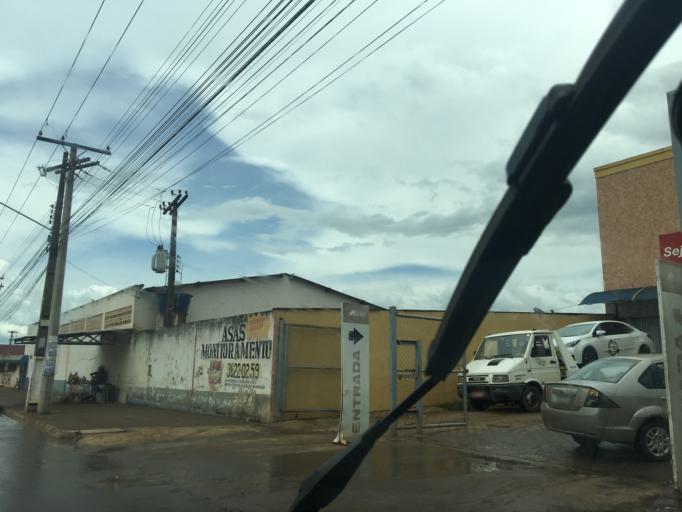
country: BR
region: Goias
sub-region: Luziania
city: Luziania
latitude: -16.2473
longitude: -47.9151
